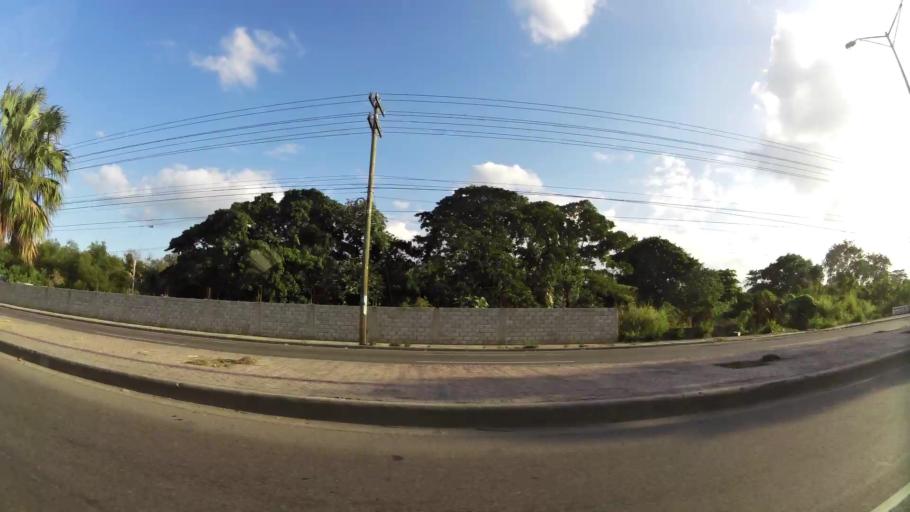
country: DO
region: Nacional
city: Ensanche Luperon
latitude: 18.5461
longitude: -69.9124
